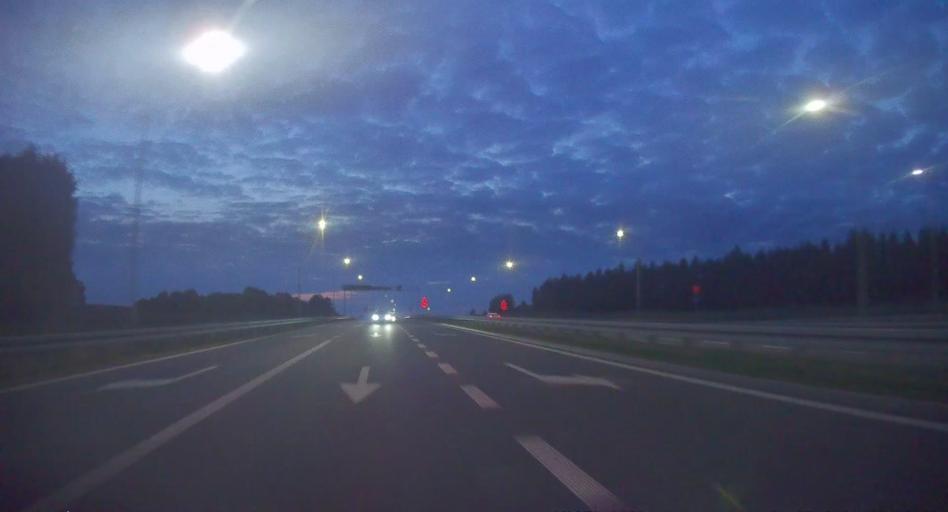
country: PL
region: Silesian Voivodeship
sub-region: Powiat klobucki
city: Kamyk
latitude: 50.8530
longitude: 19.0355
